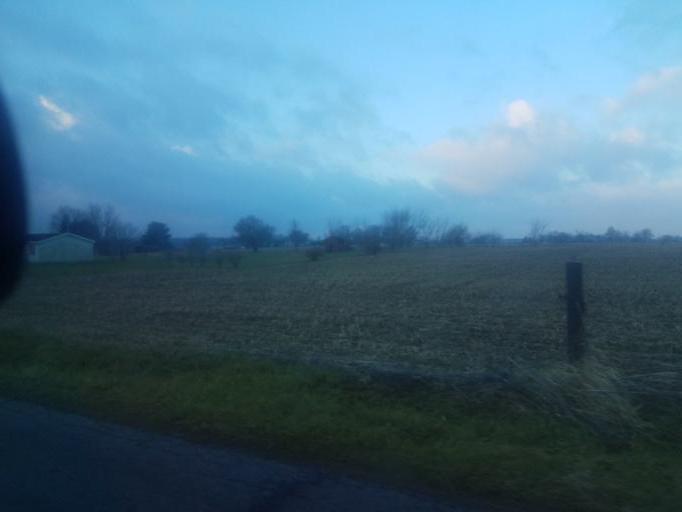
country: US
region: Ohio
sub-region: Marion County
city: Marion
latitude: 40.6321
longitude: -83.1890
